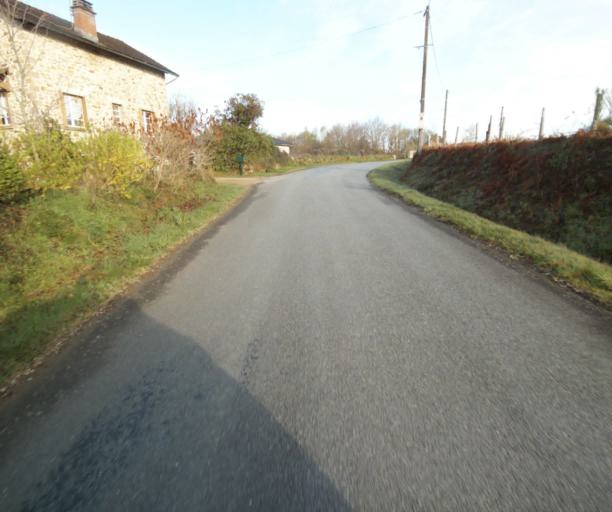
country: FR
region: Limousin
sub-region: Departement de la Correze
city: Naves
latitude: 45.3144
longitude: 1.8343
